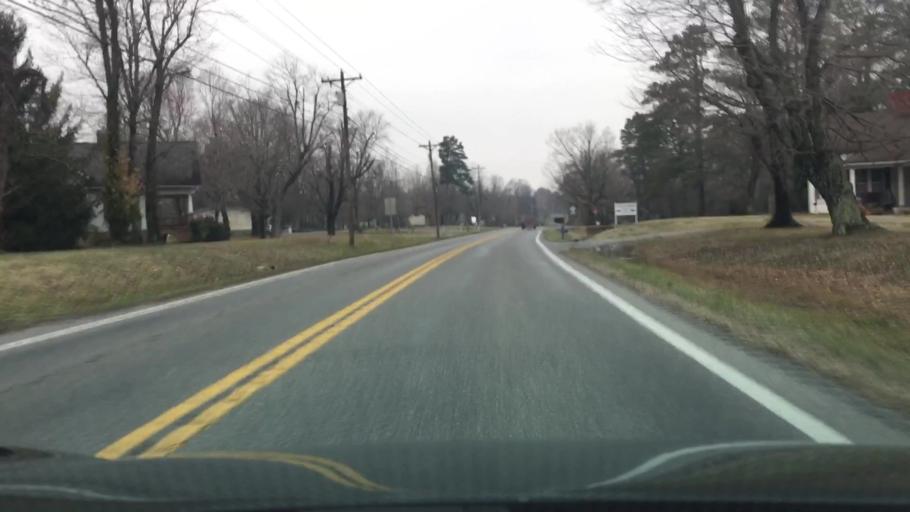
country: US
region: Kentucky
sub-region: Livingston County
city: Ledbetter
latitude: 36.9685
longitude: -88.4574
